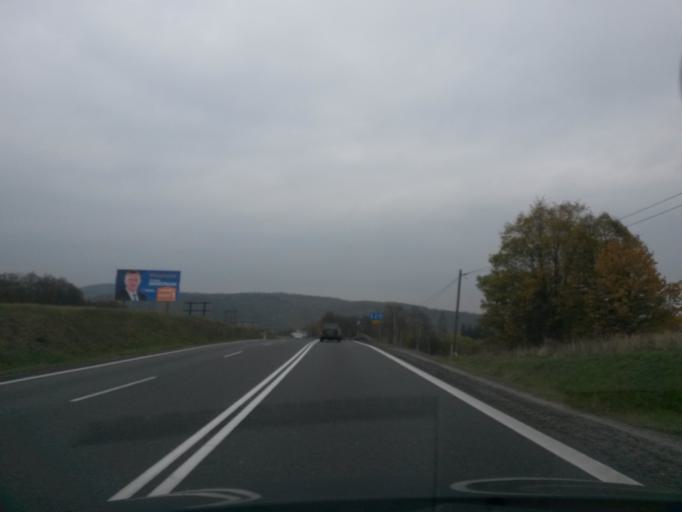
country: PL
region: Lower Silesian Voivodeship
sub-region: Powiat zabkowicki
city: Bardo
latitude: 50.4966
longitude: 16.7246
